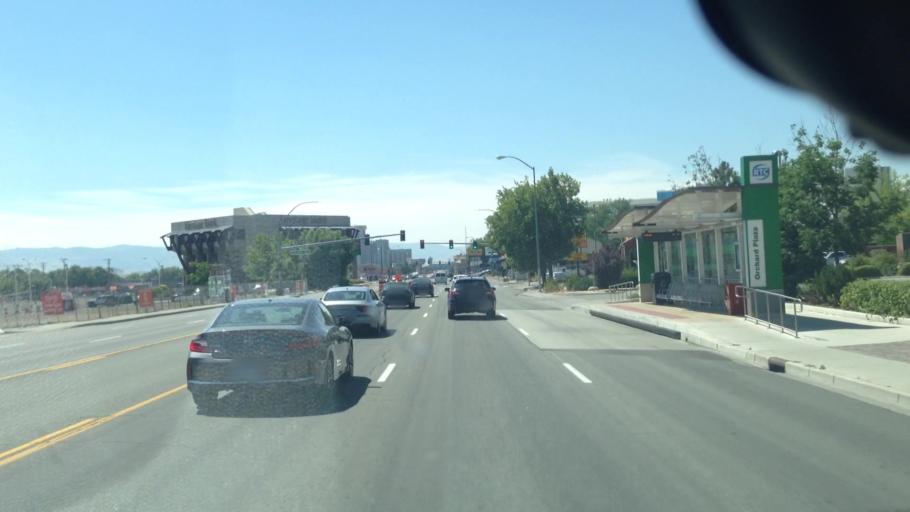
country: US
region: Nevada
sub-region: Washoe County
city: Reno
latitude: 39.5038
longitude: -119.8024
